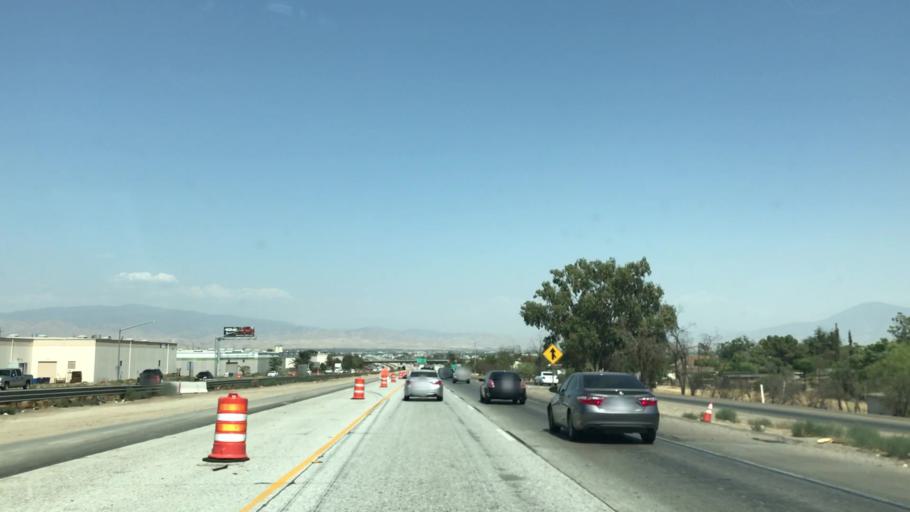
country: US
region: California
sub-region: Kern County
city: Bakersfield
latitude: 35.3523
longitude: -118.9836
